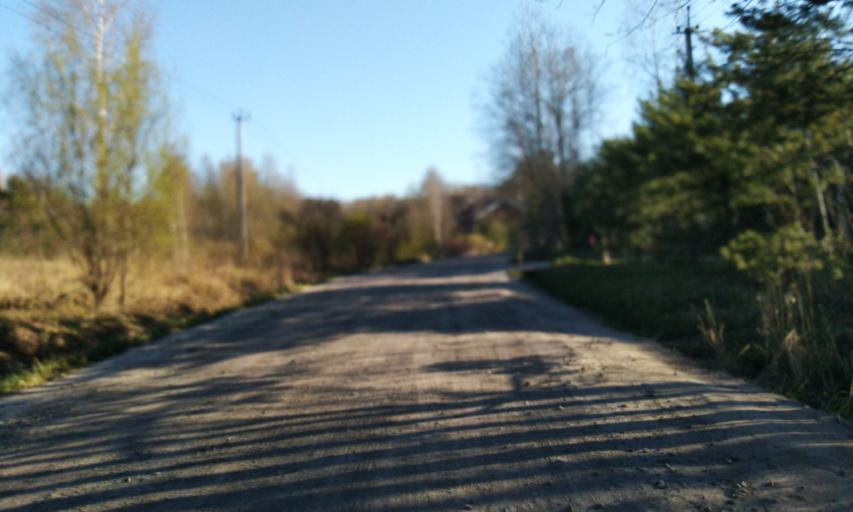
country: RU
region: Leningrad
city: Toksovo
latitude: 60.1511
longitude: 30.5817
